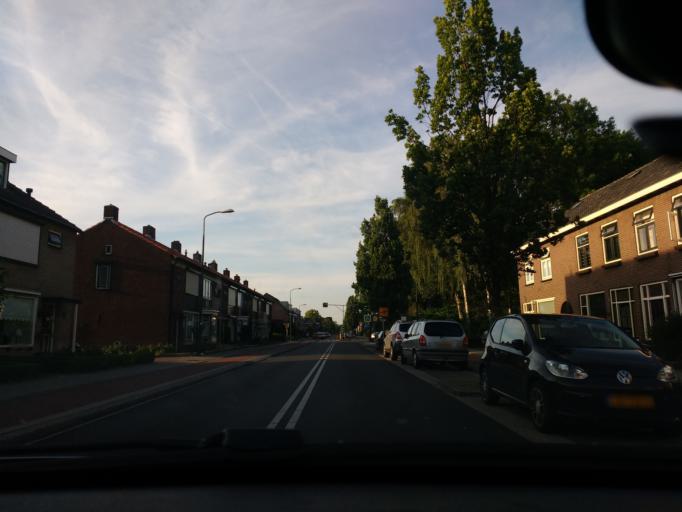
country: NL
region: Utrecht
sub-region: Gemeente Veenendaal
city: Veenendaal
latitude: 52.0328
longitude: 5.5624
